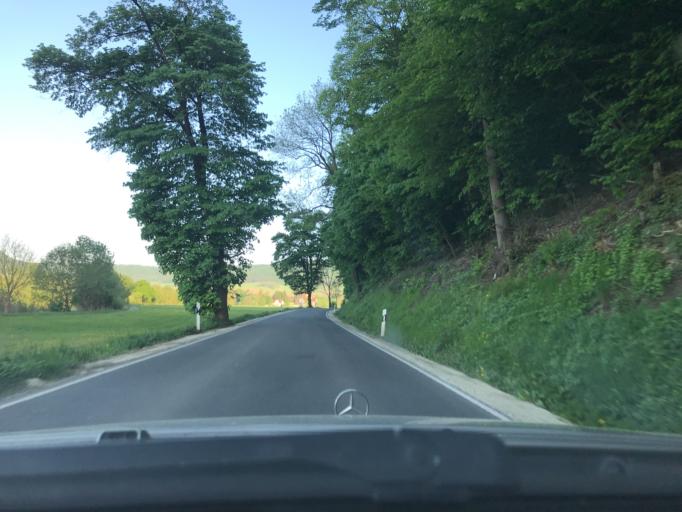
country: DE
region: Hesse
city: Wanfried
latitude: 51.1896
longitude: 10.1531
